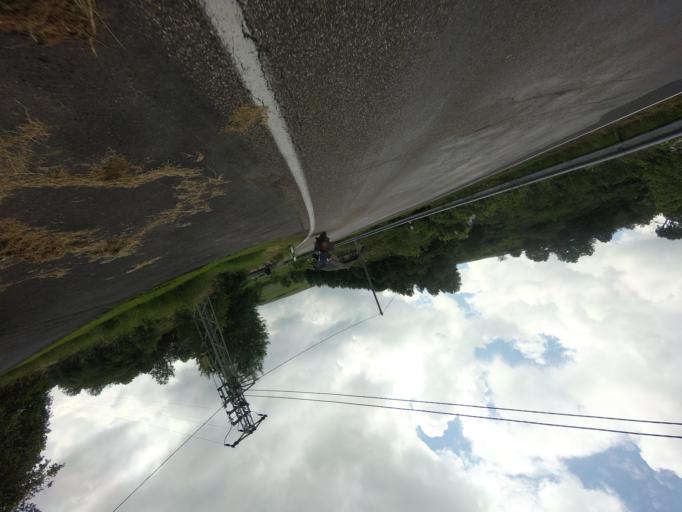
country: DE
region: Rheinland-Pfalz
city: Welschenbach
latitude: 50.3585
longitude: 7.0686
